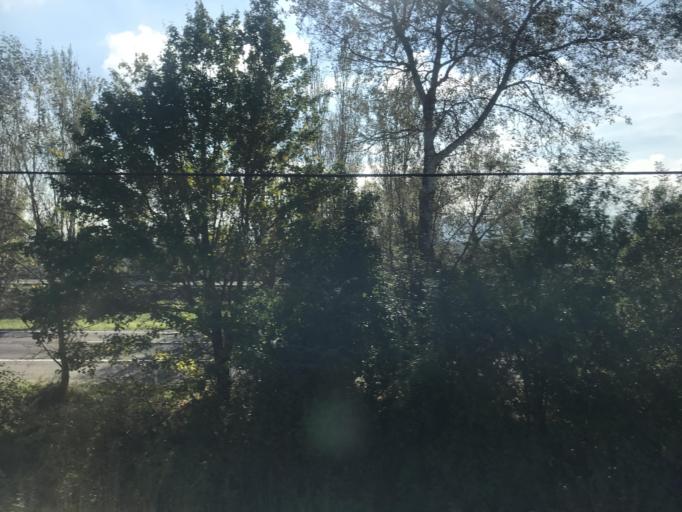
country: ES
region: Basque Country
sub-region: Provincia de Alava
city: Arminon
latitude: 42.7545
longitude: -2.8371
